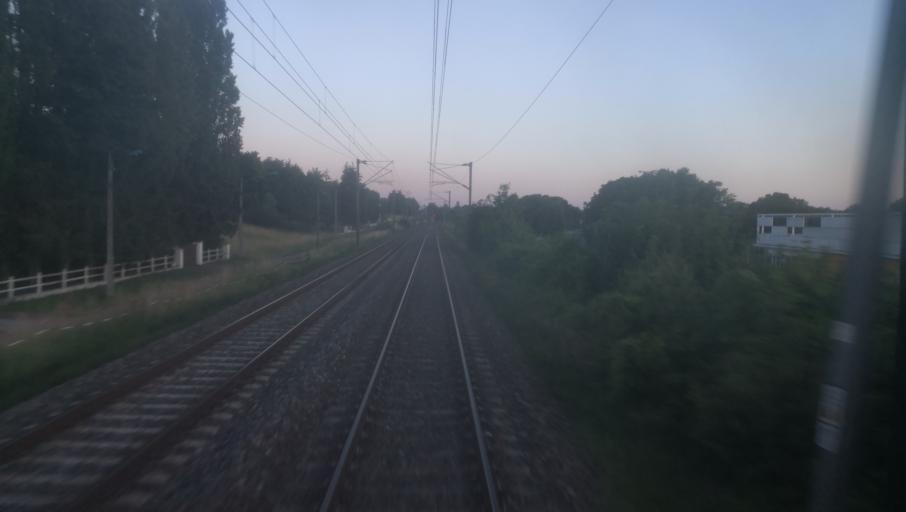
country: FR
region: Bourgogne
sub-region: Departement de la Nievre
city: Cosne-Cours-sur-Loire
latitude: 47.4260
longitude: 2.9320
